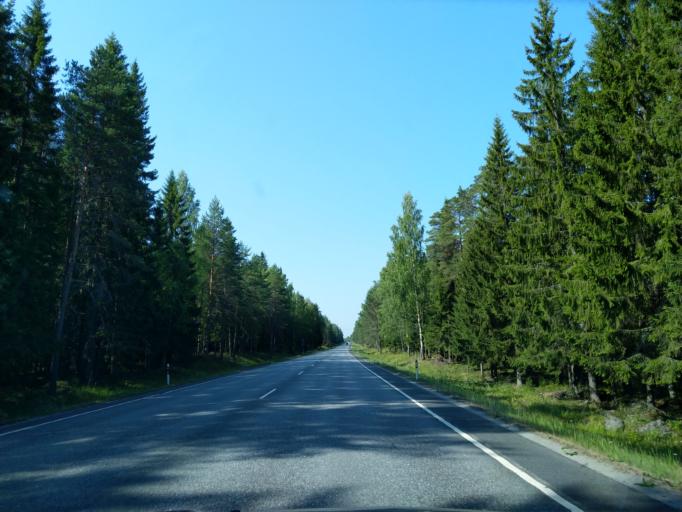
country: FI
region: Satakunta
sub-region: Pori
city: Noormarkku
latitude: 61.6252
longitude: 21.9188
